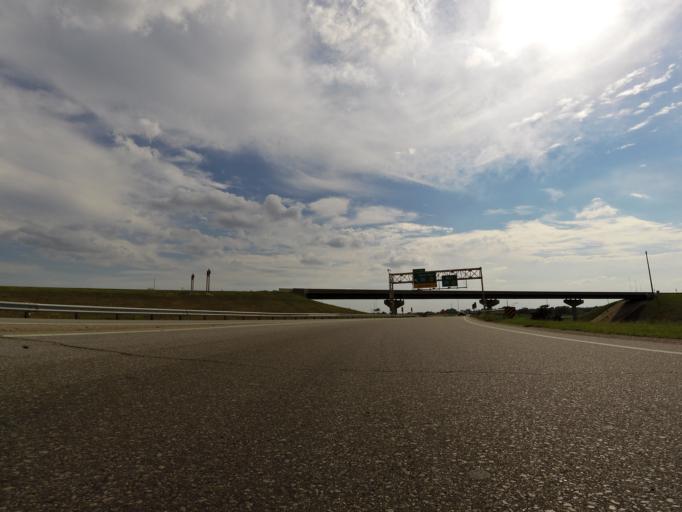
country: US
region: Kansas
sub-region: Sedgwick County
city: Park City
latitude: 37.7634
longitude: -97.3199
